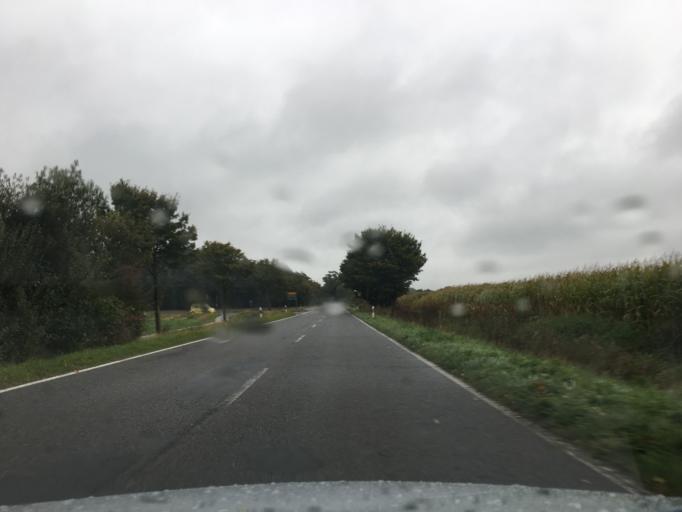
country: DE
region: Schleswig-Holstein
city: Felm
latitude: 54.3862
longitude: 10.0571
